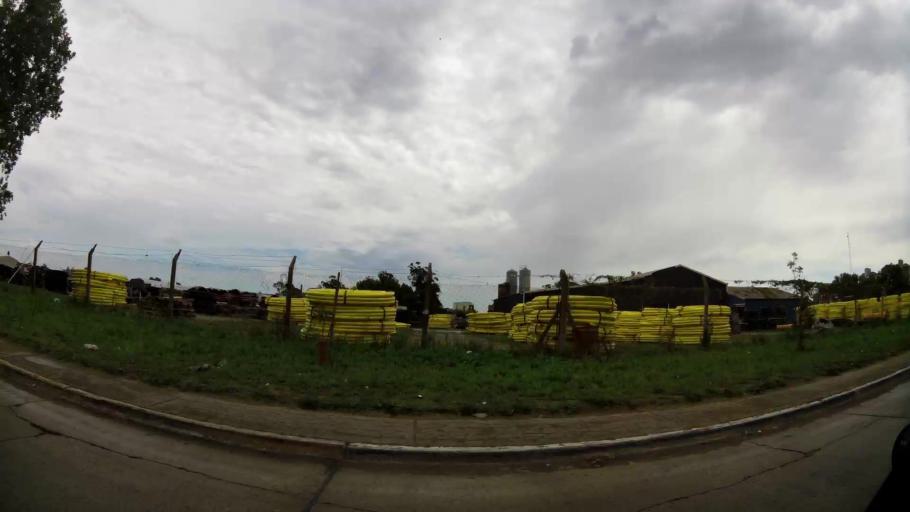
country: AR
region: Buenos Aires
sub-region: Partido de Quilmes
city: Quilmes
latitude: -34.7505
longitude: -58.2237
